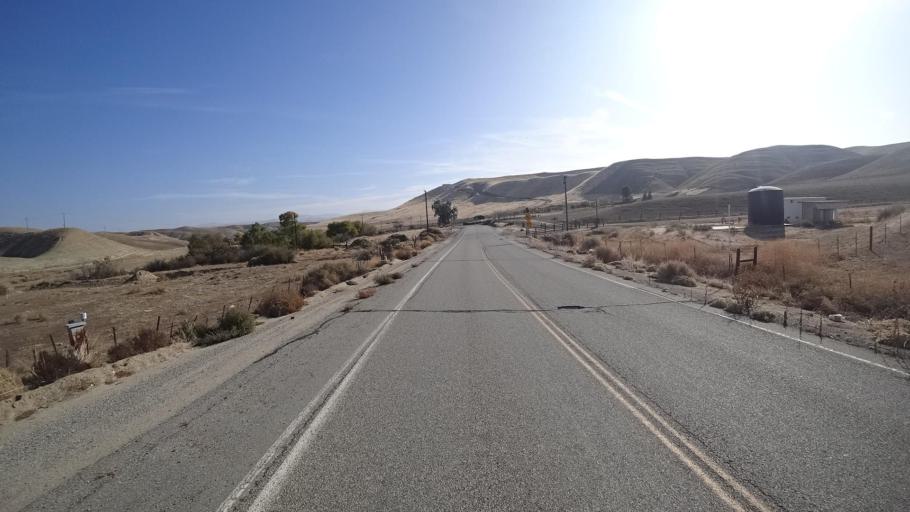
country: US
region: California
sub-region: Kern County
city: Oildale
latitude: 35.5274
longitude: -118.9723
